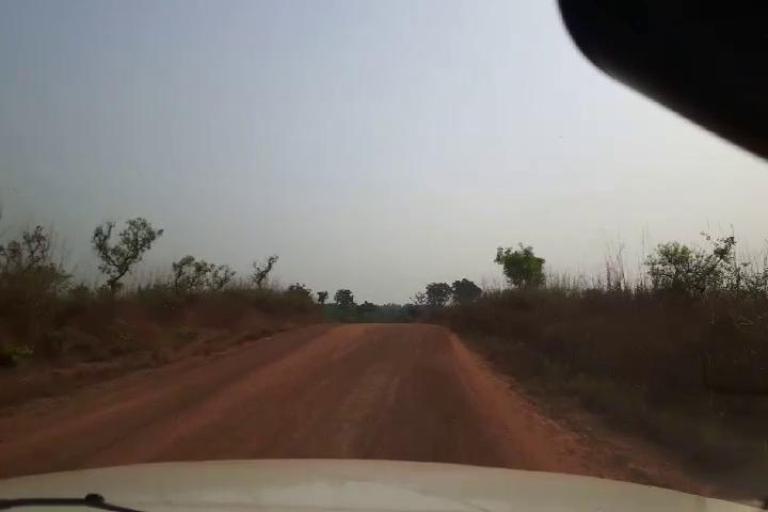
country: SL
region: Northern Province
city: Masingbi
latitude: 8.8035
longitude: -11.8635
